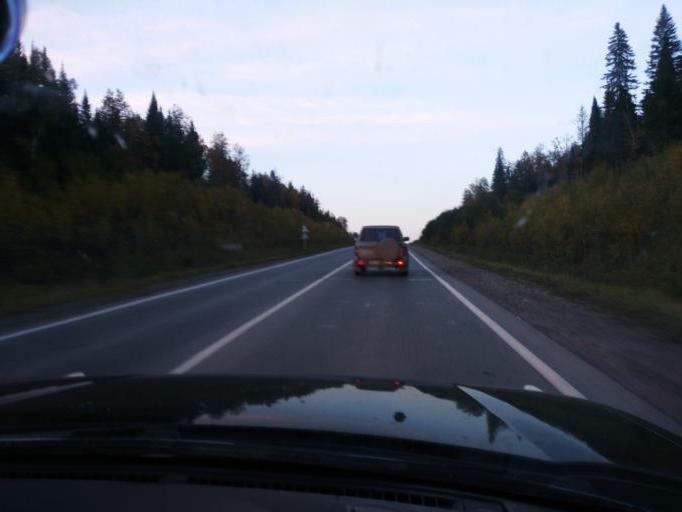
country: RU
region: Perm
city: Sylva
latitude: 58.2854
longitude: 56.7386
